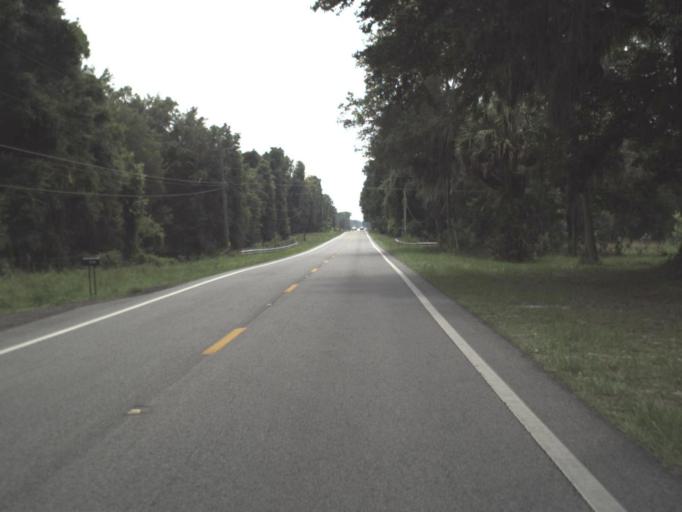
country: US
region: Florida
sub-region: Levy County
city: Chiefland
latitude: 29.4652
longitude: -82.8893
